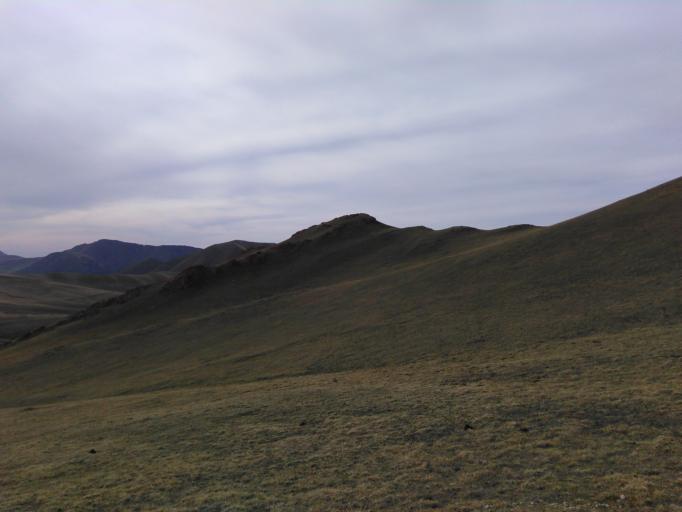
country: KG
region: Chuy
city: Bystrovka
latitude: 42.5004
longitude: 75.7187
